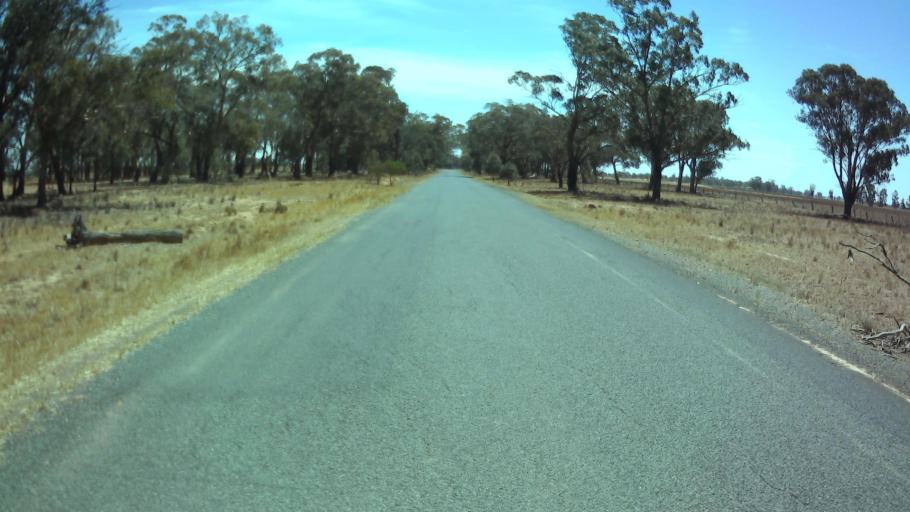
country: AU
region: New South Wales
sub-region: Weddin
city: Grenfell
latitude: -34.0027
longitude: 147.7570
